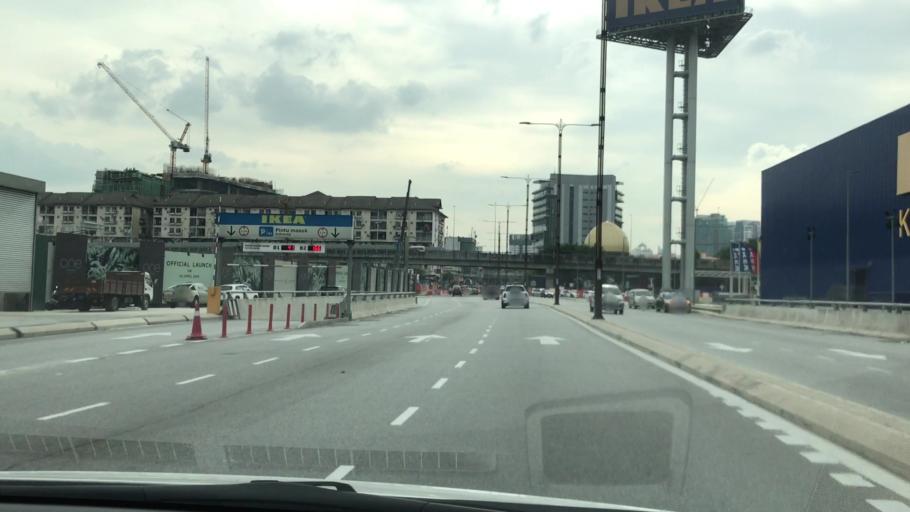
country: MY
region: Kuala Lumpur
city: Kuala Lumpur
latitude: 3.1339
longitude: 101.7212
